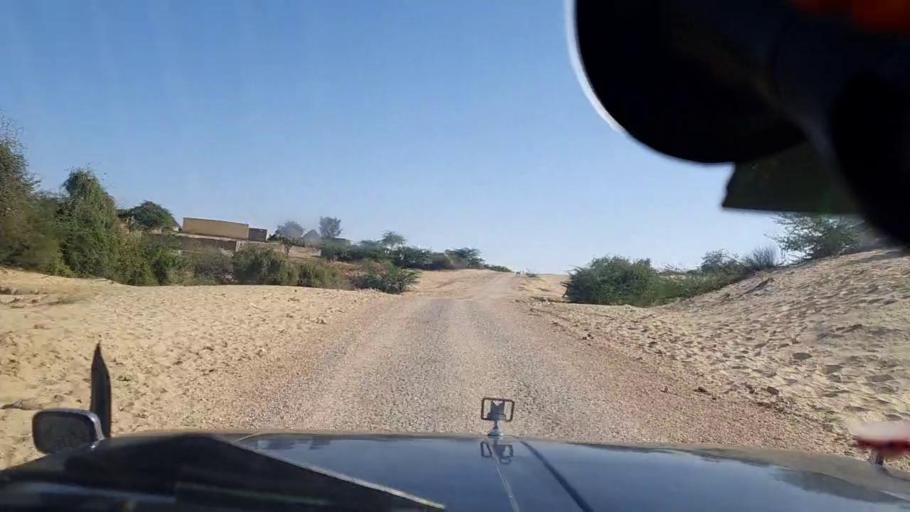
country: PK
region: Sindh
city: Diplo
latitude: 24.4720
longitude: 69.7939
